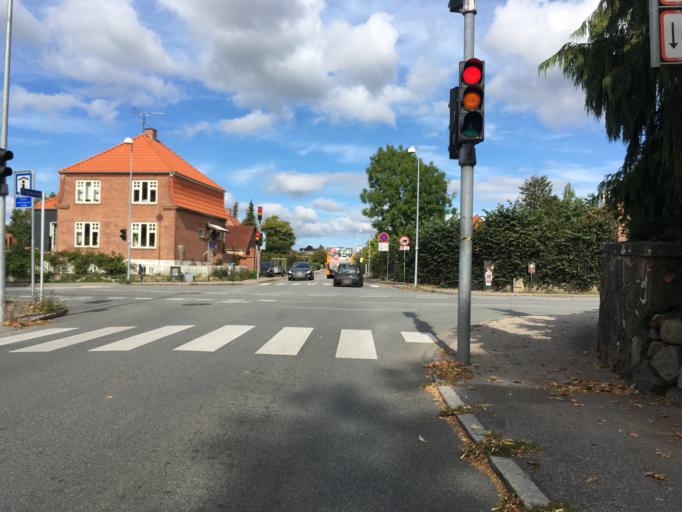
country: DK
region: Capital Region
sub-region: Hillerod Kommune
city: Hillerod
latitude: 55.9365
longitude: 12.2892
